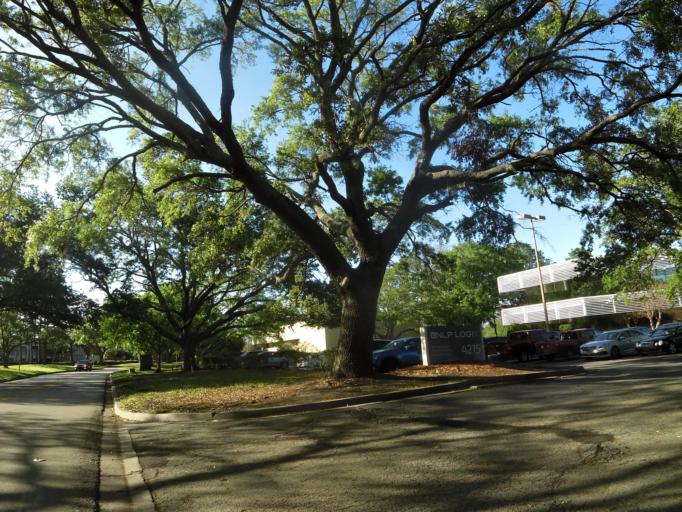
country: US
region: Florida
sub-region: Duval County
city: Jacksonville
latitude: 30.2540
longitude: -81.5887
